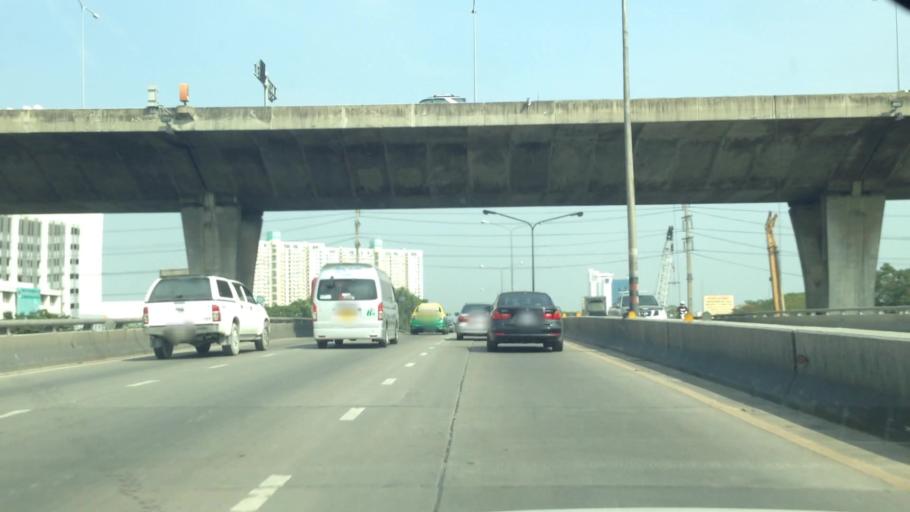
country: TH
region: Bangkok
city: Bang Na
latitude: 13.6653
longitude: 100.6442
